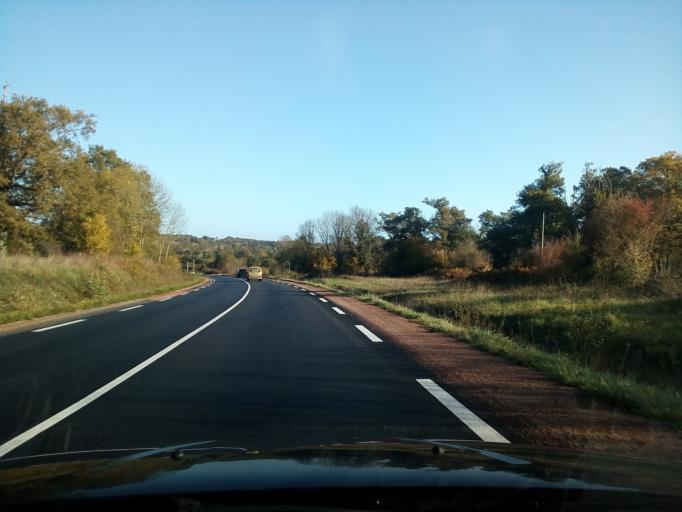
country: FR
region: Limousin
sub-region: Departement de la Haute-Vienne
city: Bellac
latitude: 46.1455
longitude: 1.1024
